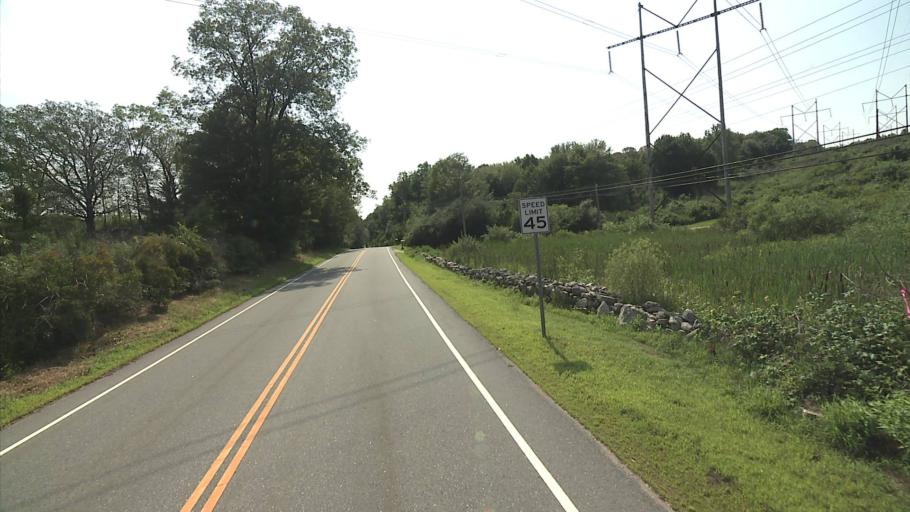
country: US
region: Connecticut
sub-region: New London County
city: Montville Center
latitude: 41.5747
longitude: -72.1868
